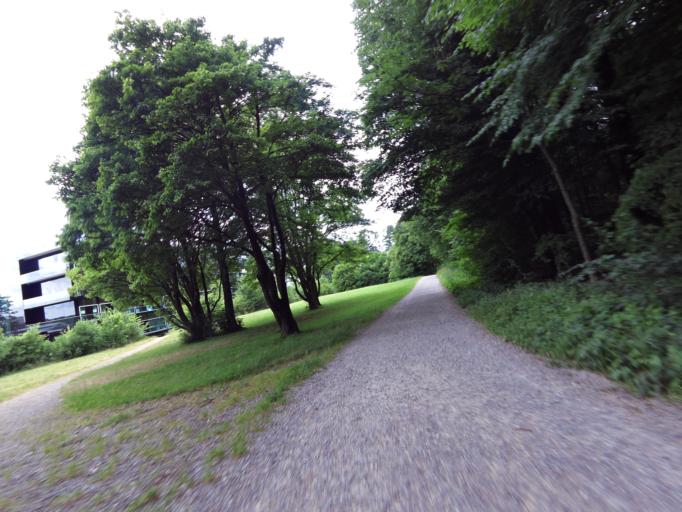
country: CH
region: Zurich
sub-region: Bezirk Zuerich
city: Zuerich (Kreis 11) / Affoltern
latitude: 47.4081
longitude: 8.5118
